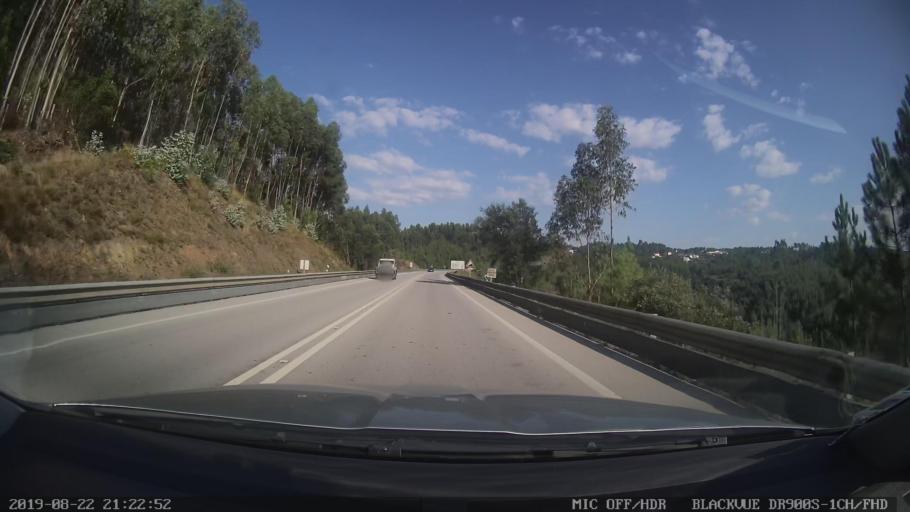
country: PT
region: Castelo Branco
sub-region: Serta
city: Serta
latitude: 39.8235
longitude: -8.1046
